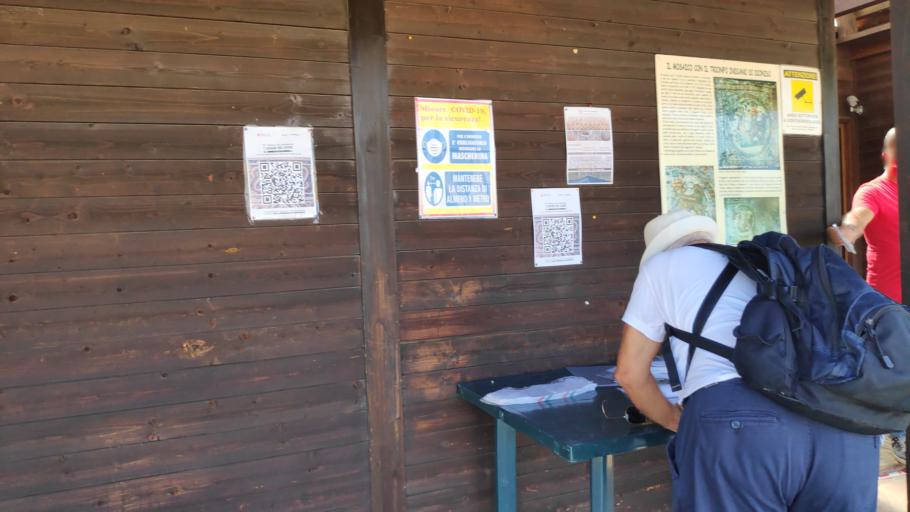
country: IT
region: Calabria
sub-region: Provincia di Reggio Calabria
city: Bianco
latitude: 38.1188
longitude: 16.1583
